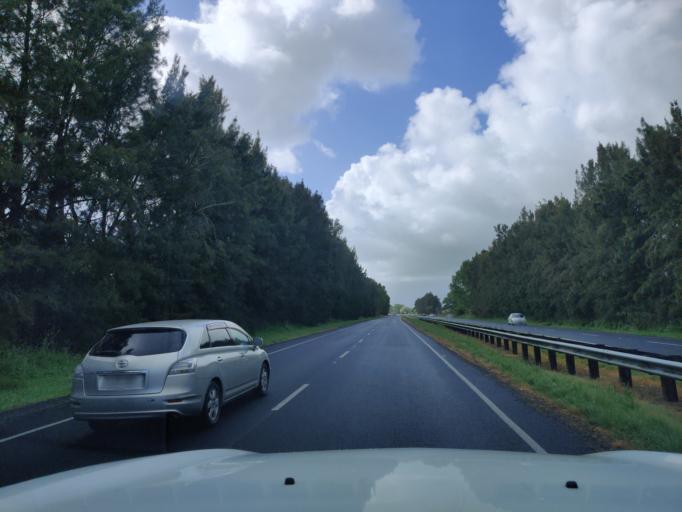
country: NZ
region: Waikato
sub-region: Waipa District
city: Cambridge
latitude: -37.8338
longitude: 175.3630
